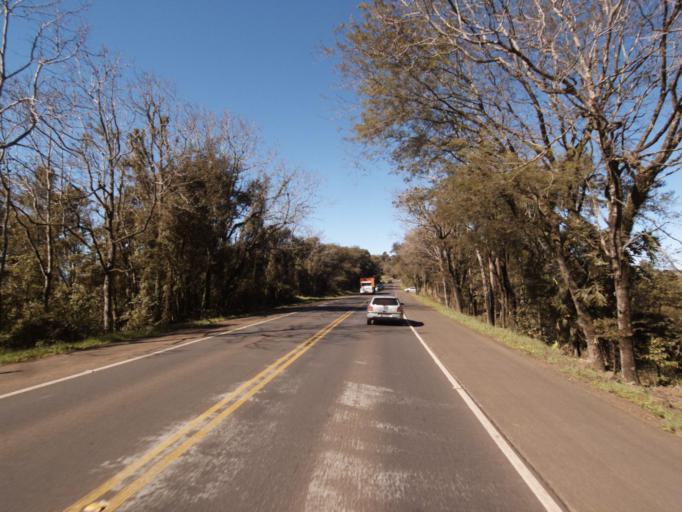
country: BR
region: Santa Catarina
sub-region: Chapeco
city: Chapeco
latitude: -26.8991
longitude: -52.8733
